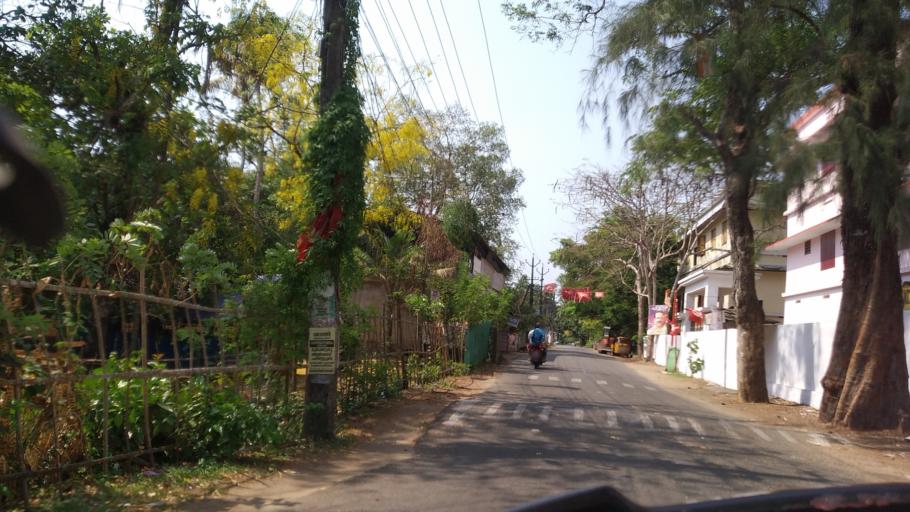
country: IN
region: Kerala
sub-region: Thrissur District
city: Irinjalakuda
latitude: 10.3165
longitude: 76.1258
